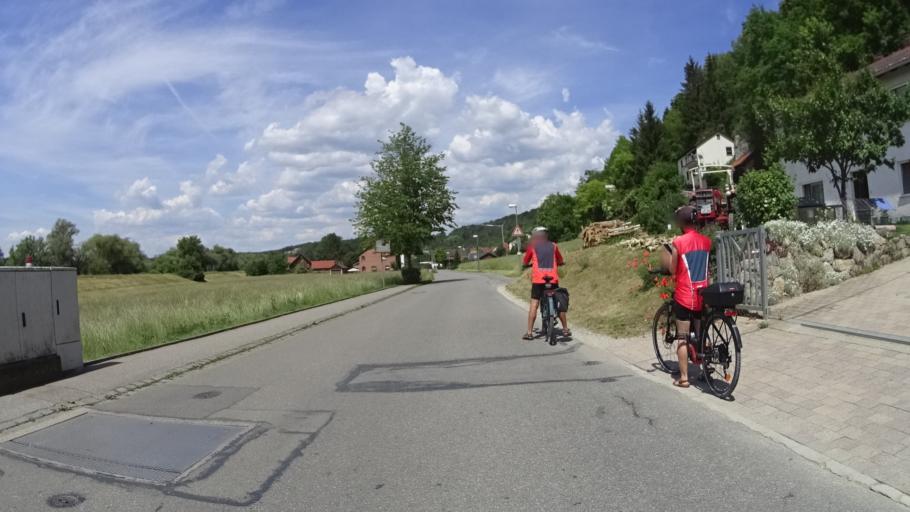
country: DE
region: Bavaria
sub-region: Lower Bavaria
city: Bad Abbach
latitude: 48.9441
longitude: 12.0277
